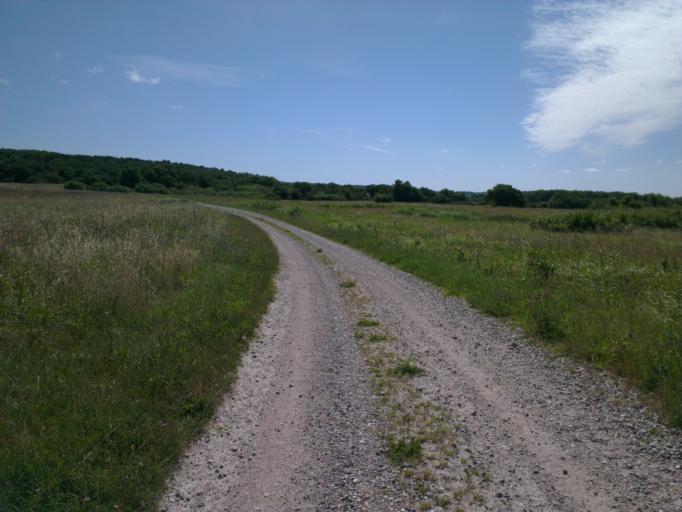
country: DK
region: Capital Region
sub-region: Frederikssund Kommune
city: Jaegerspris
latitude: 55.8769
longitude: 11.9402
